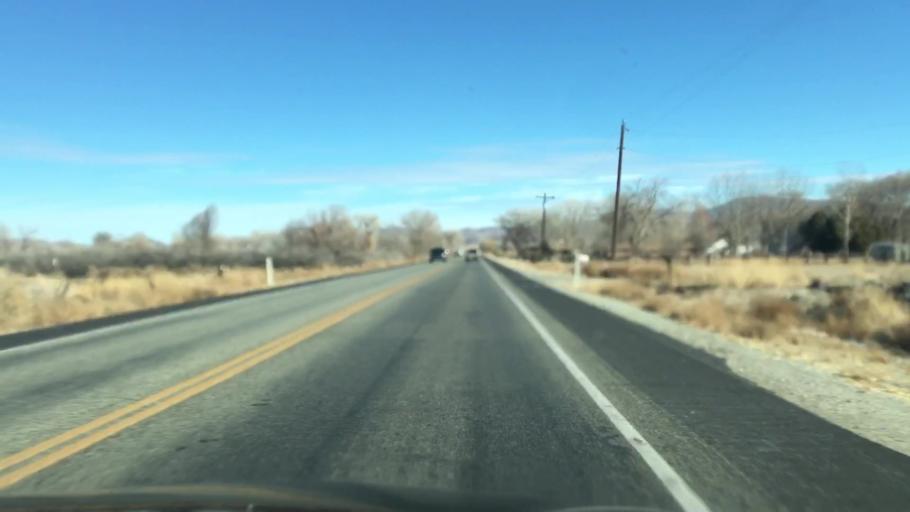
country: US
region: Nevada
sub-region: Lyon County
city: Yerington
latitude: 38.9975
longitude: -119.1496
